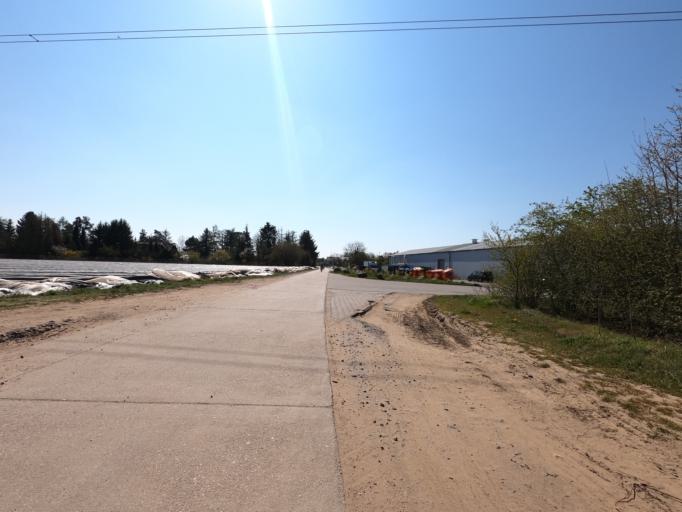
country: DE
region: Hesse
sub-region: Regierungsbezirk Darmstadt
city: Buttelborn
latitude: 49.9275
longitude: 8.5161
